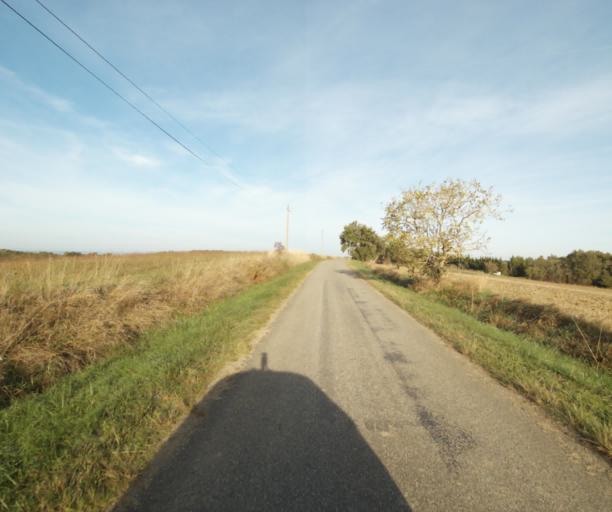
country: FR
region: Midi-Pyrenees
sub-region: Departement de la Haute-Garonne
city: Villemur-sur-Tarn
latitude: 43.9094
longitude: 1.4810
